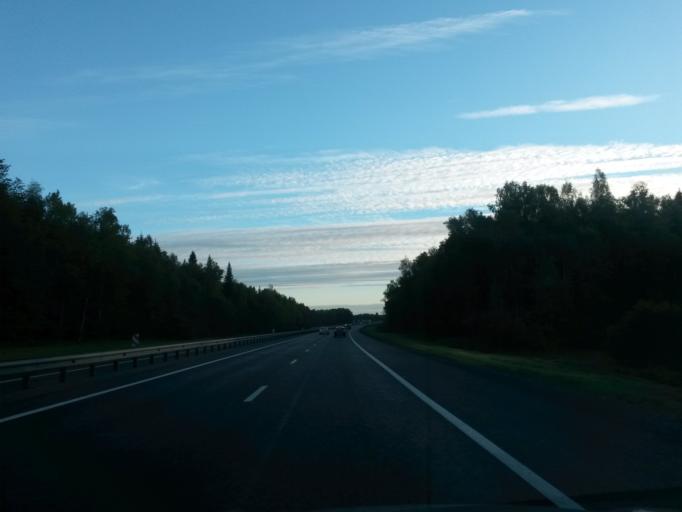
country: RU
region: Moskovskaya
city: Svatkovo
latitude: 56.4135
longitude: 38.3292
